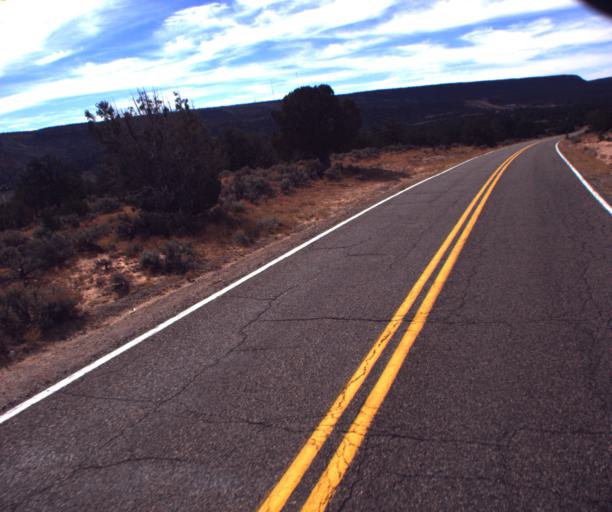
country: US
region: Arizona
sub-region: Navajo County
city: Kayenta
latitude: 36.5762
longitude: -110.4928
